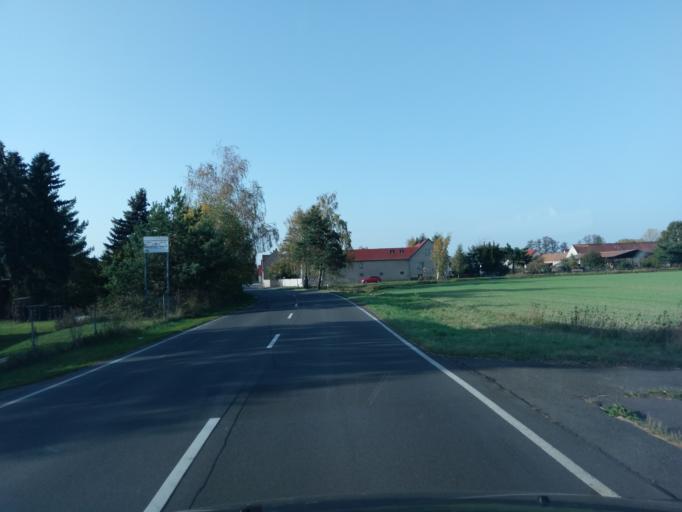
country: DE
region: Brandenburg
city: Falkenberg
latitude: 51.5392
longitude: 13.2846
